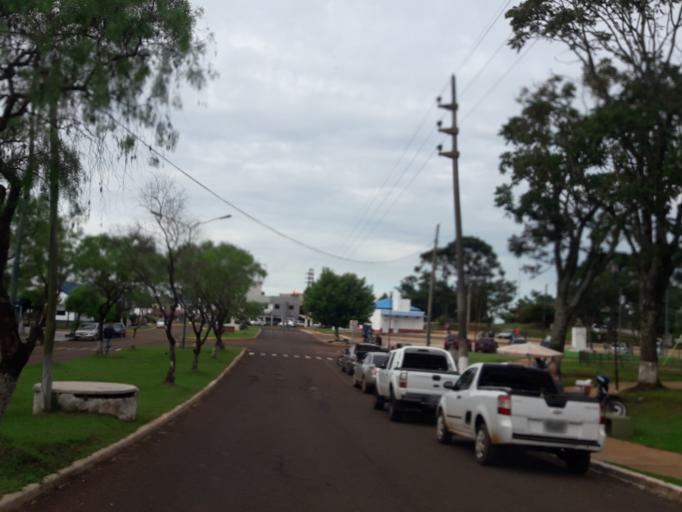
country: AR
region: Misiones
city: Bernardo de Irigoyen
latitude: -26.2558
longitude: -53.6466
